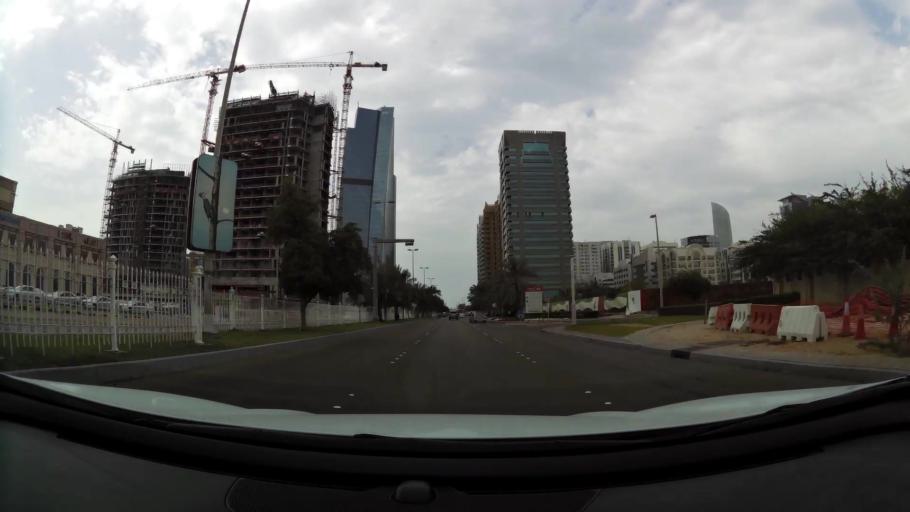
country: AE
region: Abu Dhabi
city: Abu Dhabi
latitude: 24.4714
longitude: 54.3523
